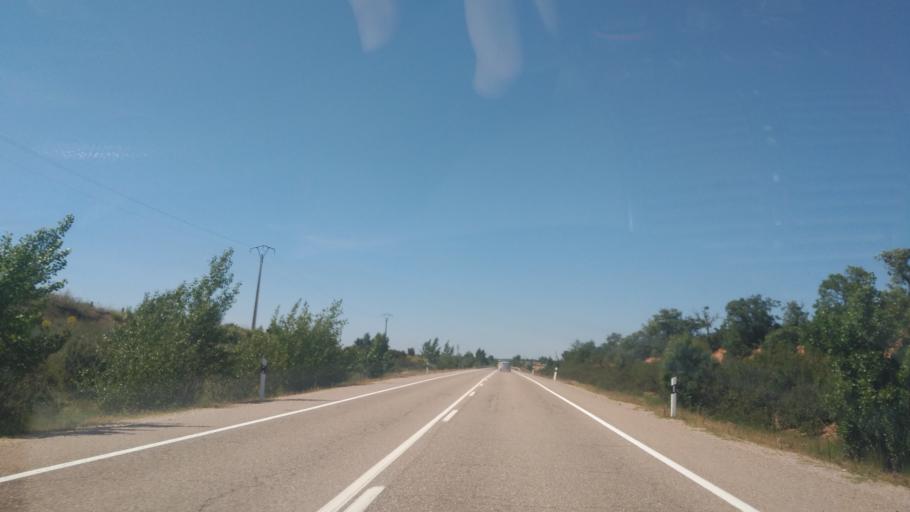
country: ES
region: Castille and Leon
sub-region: Provincia de Salamanca
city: Topas
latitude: 41.1825
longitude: -5.6946
